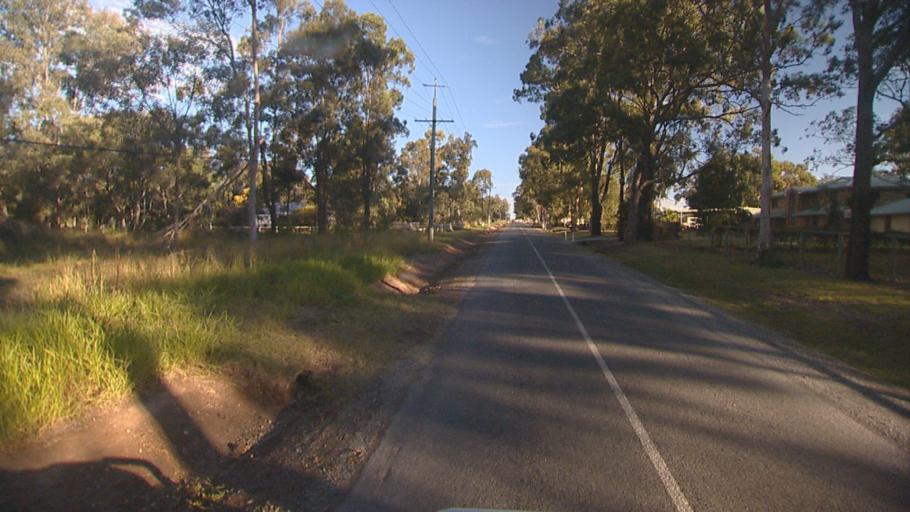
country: AU
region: Queensland
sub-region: Logan
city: Waterford West
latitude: -27.7195
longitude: 153.1485
